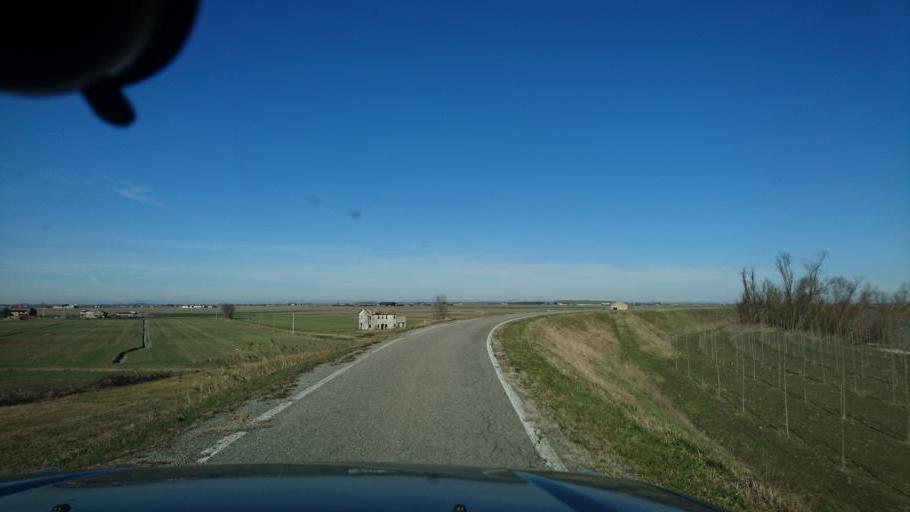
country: IT
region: Veneto
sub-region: Provincia di Rovigo
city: Ariano
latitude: 44.9347
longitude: 12.1576
